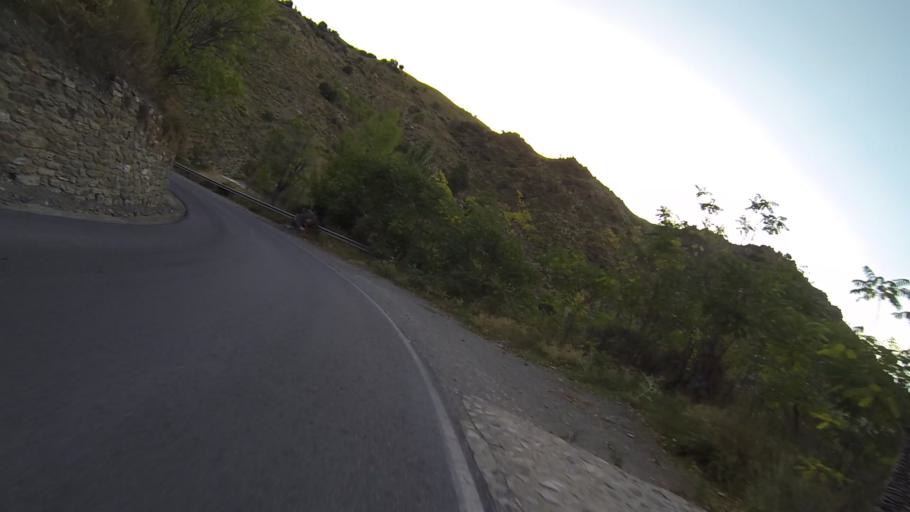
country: ES
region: Andalusia
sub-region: Provincia de Granada
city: Berchules
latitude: 36.9876
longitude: -3.1508
